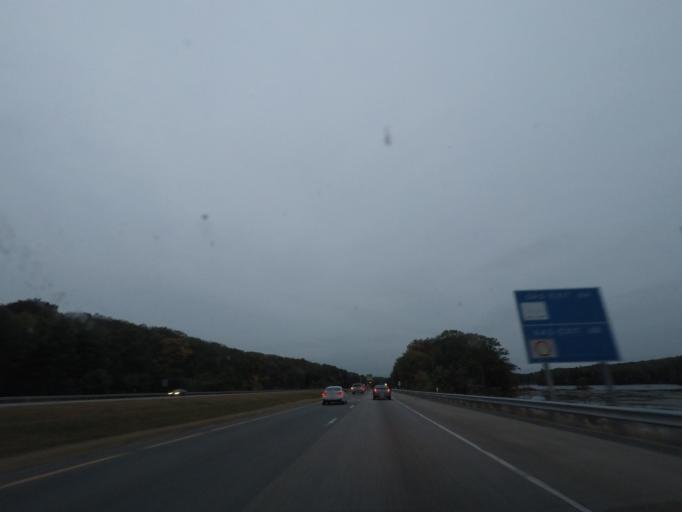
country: US
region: Massachusetts
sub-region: Worcester County
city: Auburn
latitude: 42.1760
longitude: -71.8446
